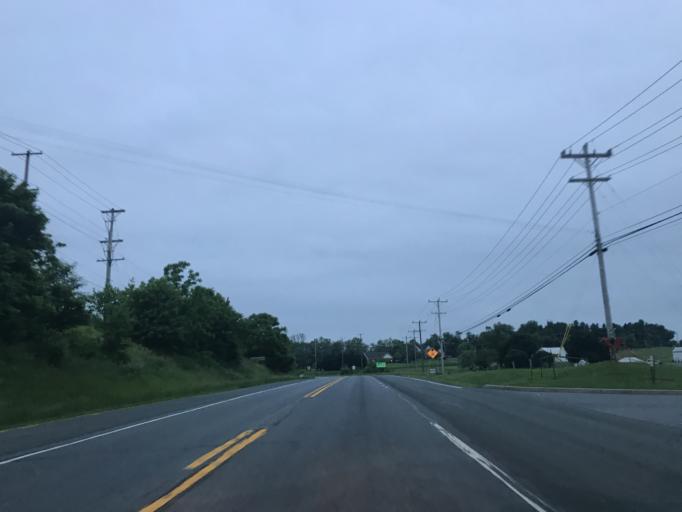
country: US
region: Maryland
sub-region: Frederick County
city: Linganore
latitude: 39.3940
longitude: -77.2616
